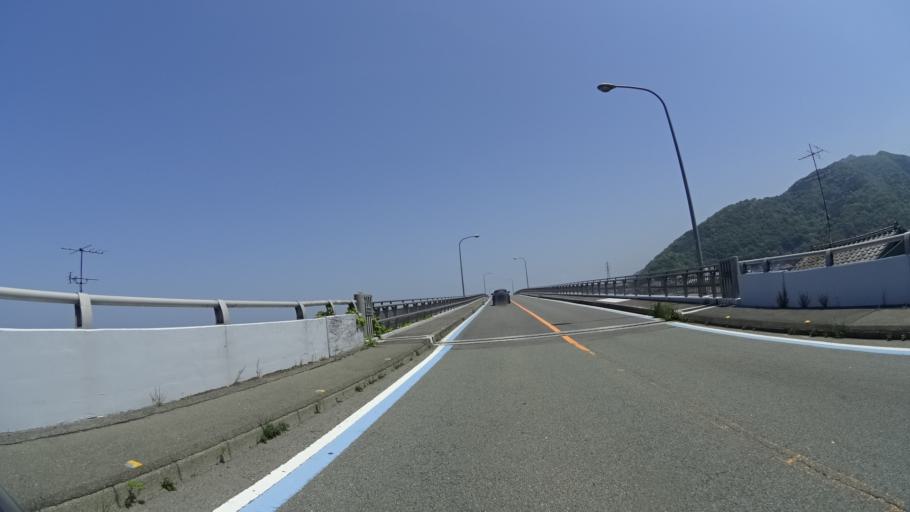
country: JP
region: Ehime
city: Ozu
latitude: 33.6106
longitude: 132.4761
